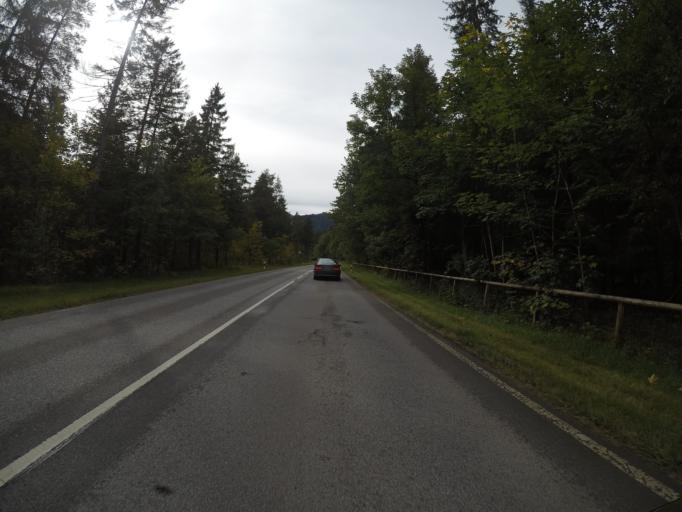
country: DE
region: Bavaria
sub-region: Upper Bavaria
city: Kreuth
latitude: 47.6337
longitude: 11.7460
